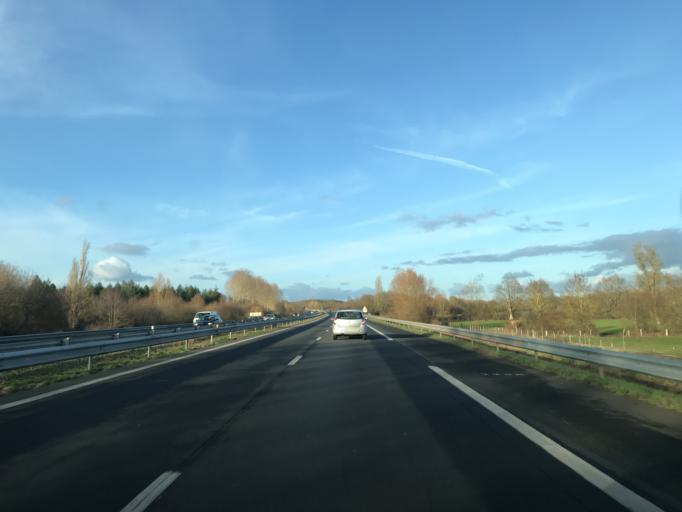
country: FR
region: Pays de la Loire
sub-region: Departement de Maine-et-Loire
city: Durtal
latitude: 47.6928
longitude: -0.2495
